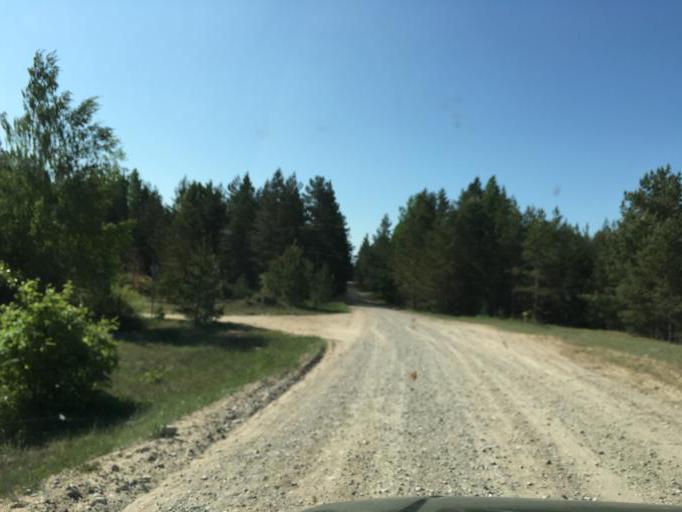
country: LV
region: Ventspils
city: Ventspils
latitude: 57.5527
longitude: 21.8586
